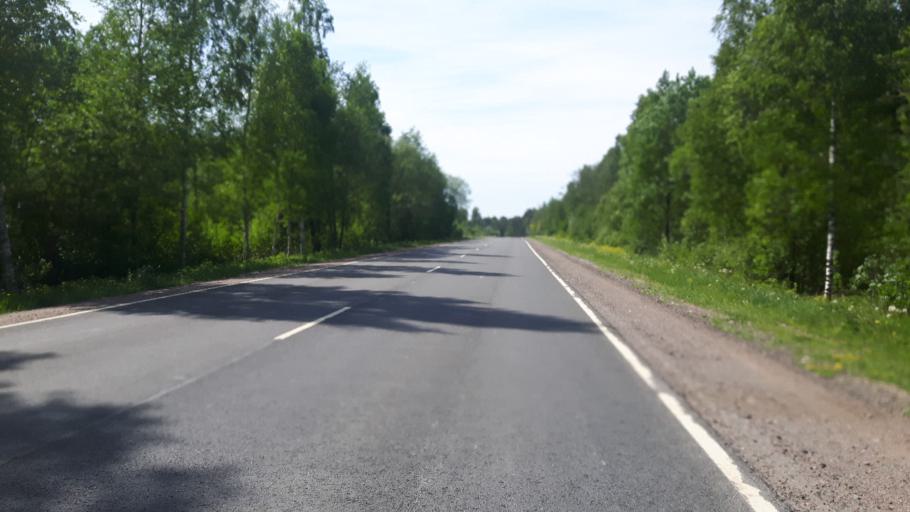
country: RU
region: Leningrad
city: Vistino
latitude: 59.6762
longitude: 28.4522
